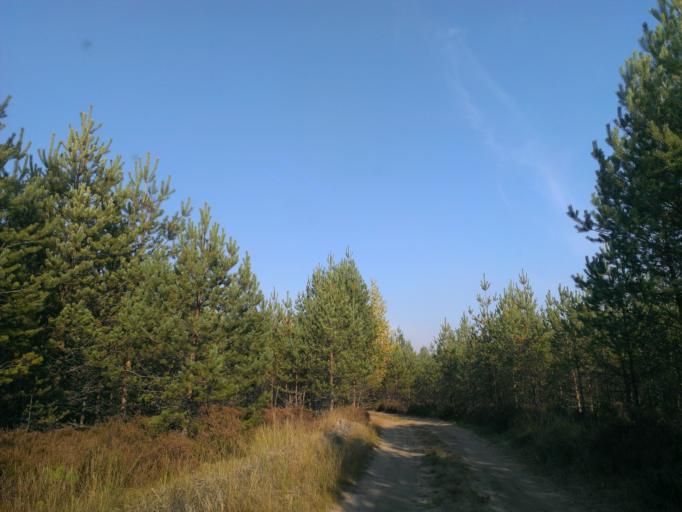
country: LV
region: Garkalne
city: Garkalne
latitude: 57.0222
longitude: 24.4872
